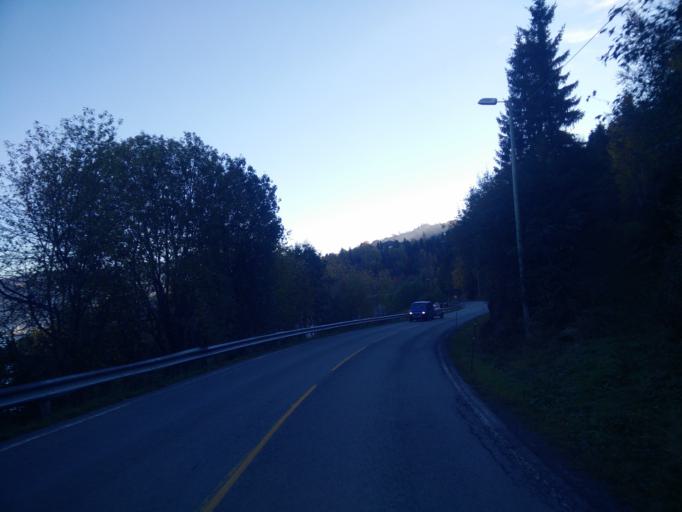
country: NO
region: Sor-Trondelag
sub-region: Skaun
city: Borsa
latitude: 63.3412
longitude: 10.0571
